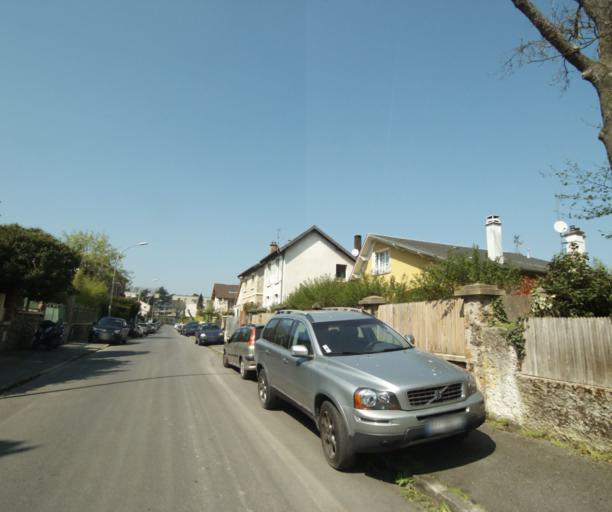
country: FR
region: Ile-de-France
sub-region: Departement des Hauts-de-Seine
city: Sevres
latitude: 48.8175
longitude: 2.2195
